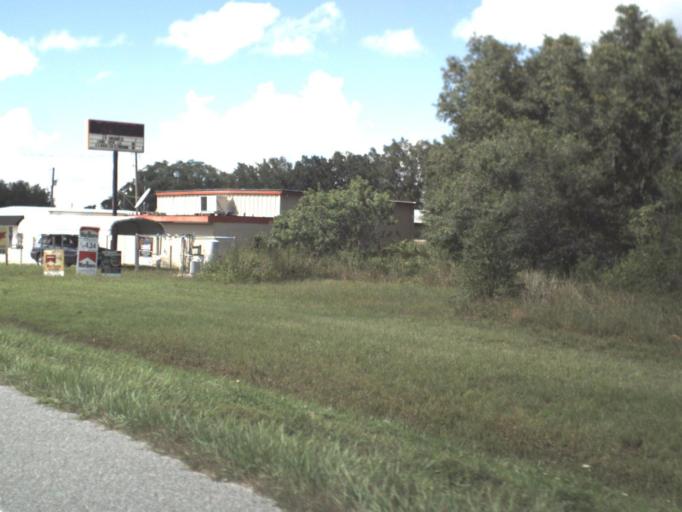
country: US
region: Florida
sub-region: Sarasota County
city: Lake Sarasota
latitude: 27.3530
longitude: -82.1704
